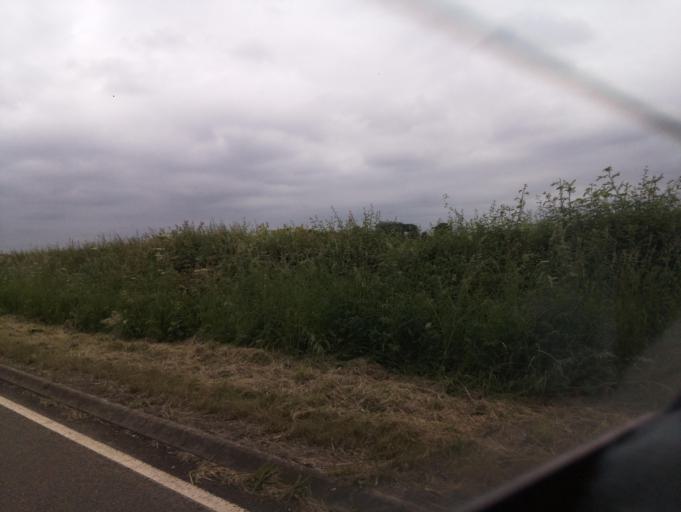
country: GB
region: England
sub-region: Leicestershire
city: Melton Mowbray
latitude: 52.7340
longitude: -0.8500
